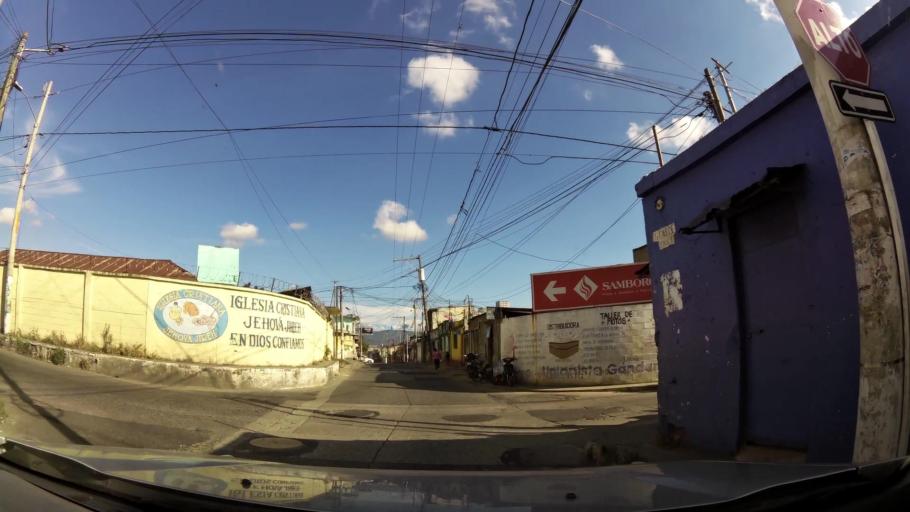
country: GT
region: Guatemala
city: Villa Nueva
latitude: 14.5238
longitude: -90.5812
